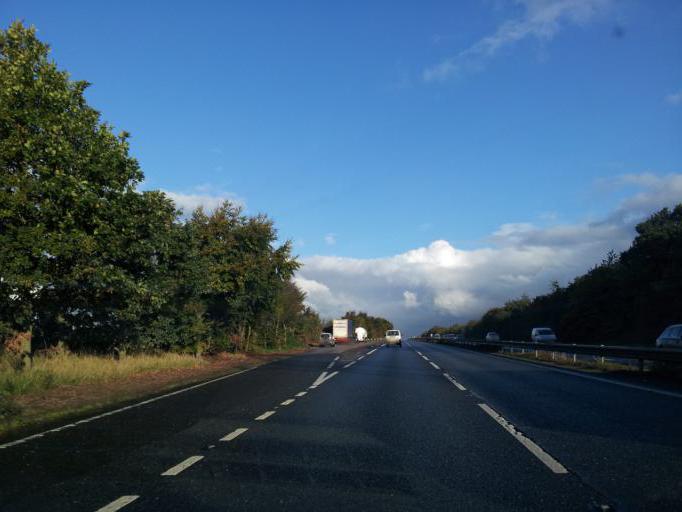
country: GB
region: England
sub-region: Norfolk
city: Costessey
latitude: 52.6416
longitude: 1.1926
